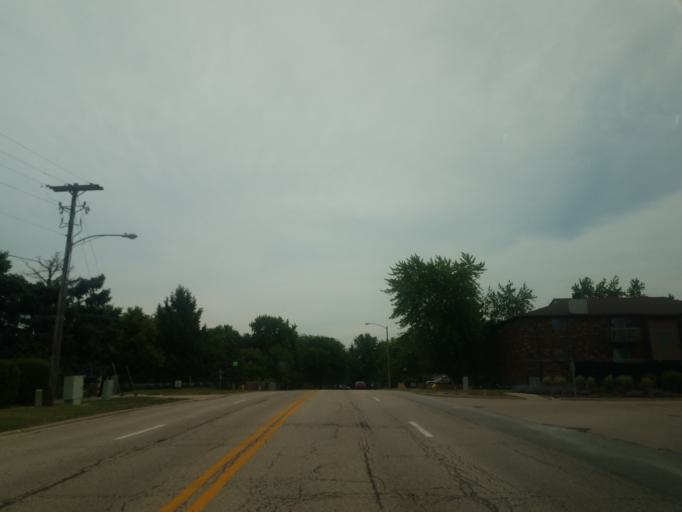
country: US
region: Illinois
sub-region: McLean County
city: Normal
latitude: 40.5002
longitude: -88.9387
